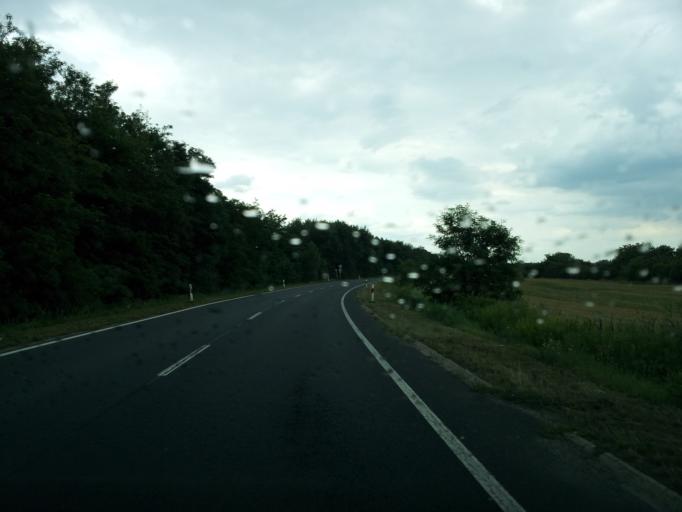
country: HU
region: Zala
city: Turje
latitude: 47.1010
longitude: 16.9965
